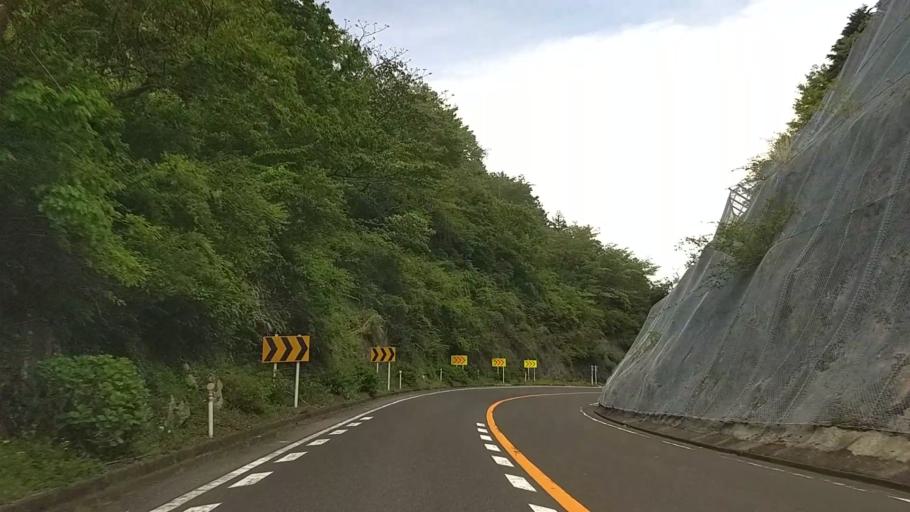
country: JP
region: Kanagawa
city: Odawara
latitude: 35.2145
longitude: 139.1059
